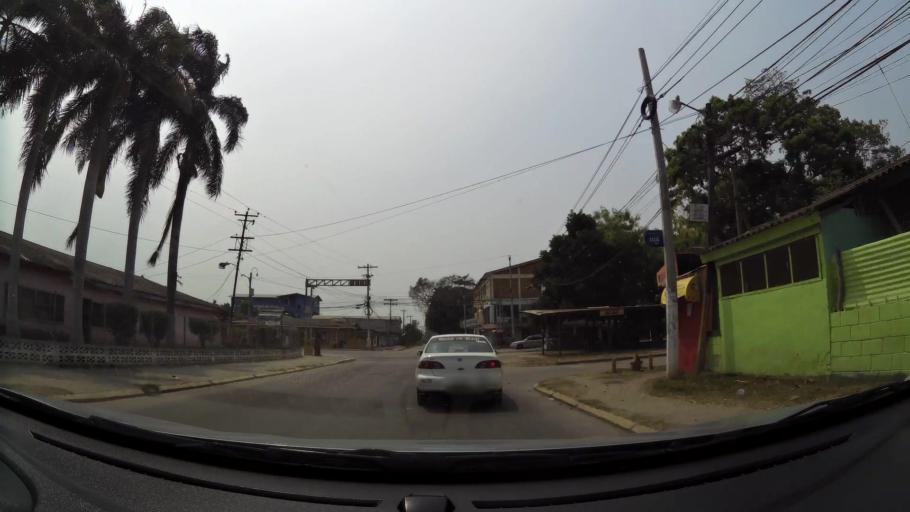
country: HN
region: Cortes
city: La Lima
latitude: 15.4411
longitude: -87.9277
